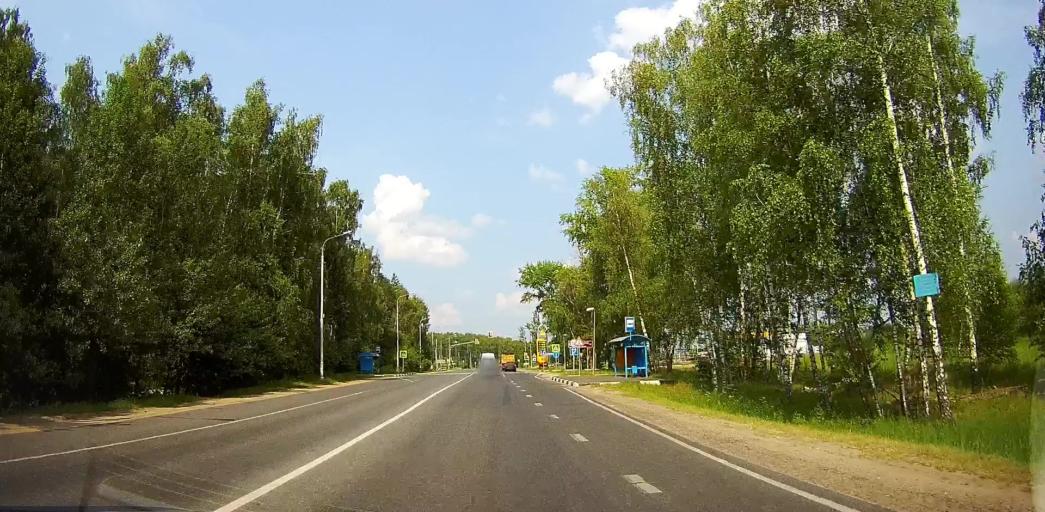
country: RU
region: Moskovskaya
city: Stupino
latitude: 54.9252
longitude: 38.1166
